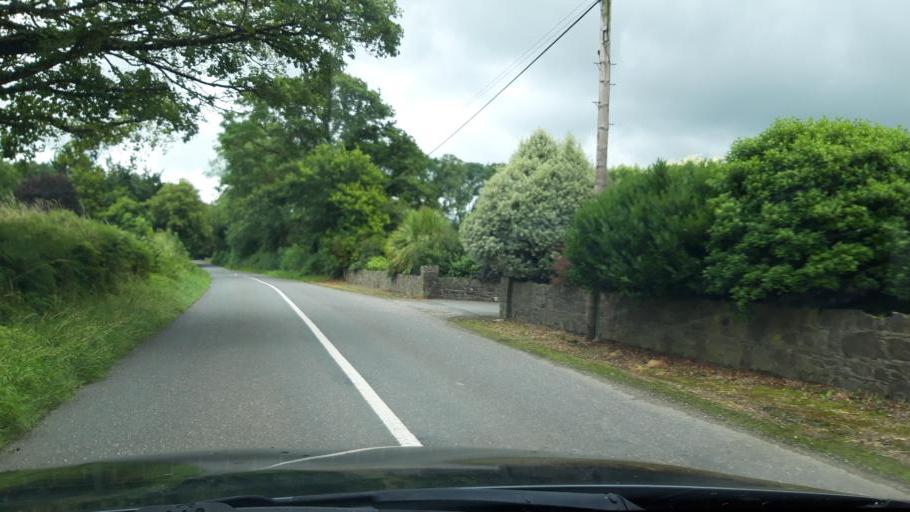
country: IE
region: Munster
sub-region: County Cork
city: Youghal
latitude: 52.1305
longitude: -7.9884
